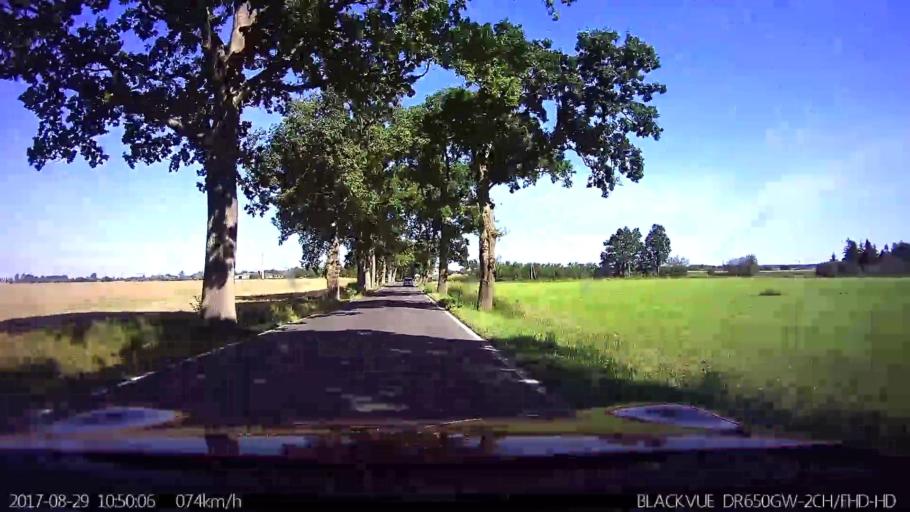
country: DE
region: Mecklenburg-Vorpommern
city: Velgast
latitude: 54.2559
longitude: 12.8219
